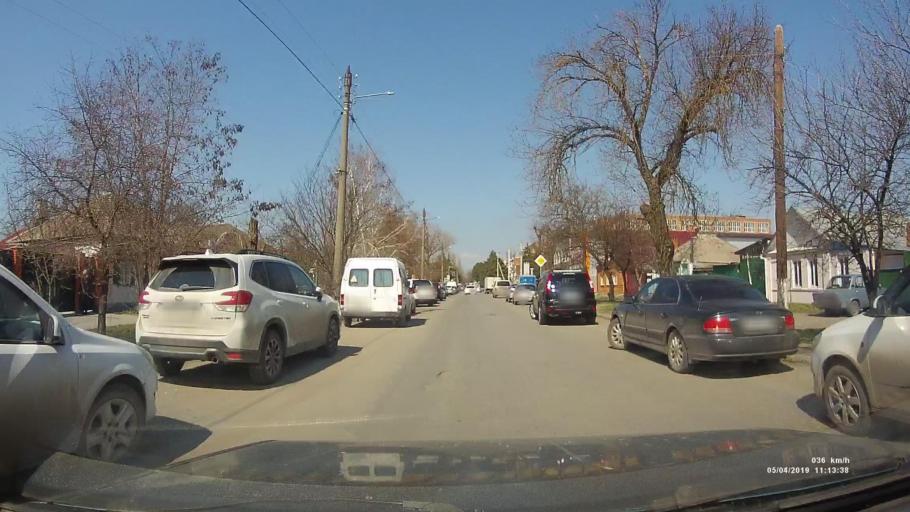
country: RU
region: Rostov
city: Azov
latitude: 47.1031
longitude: 39.4300
